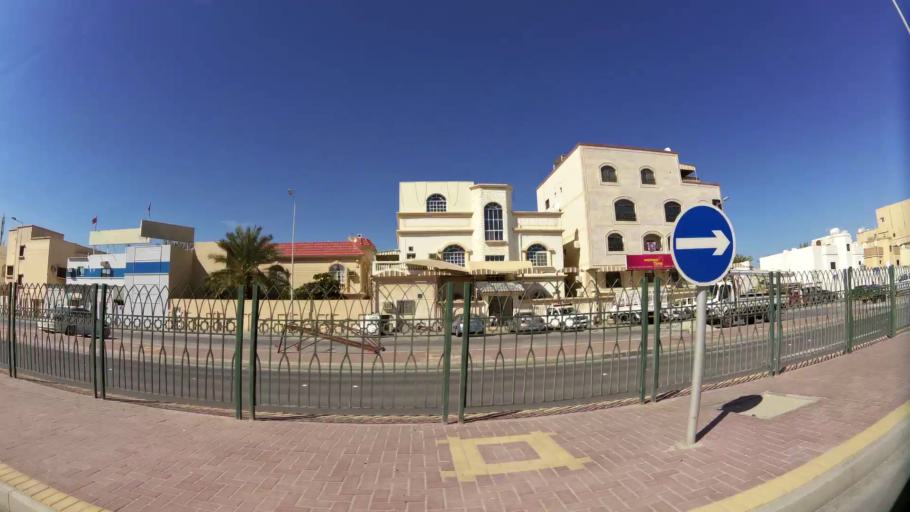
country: BH
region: Muharraq
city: Al Hadd
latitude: 26.2565
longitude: 50.6415
